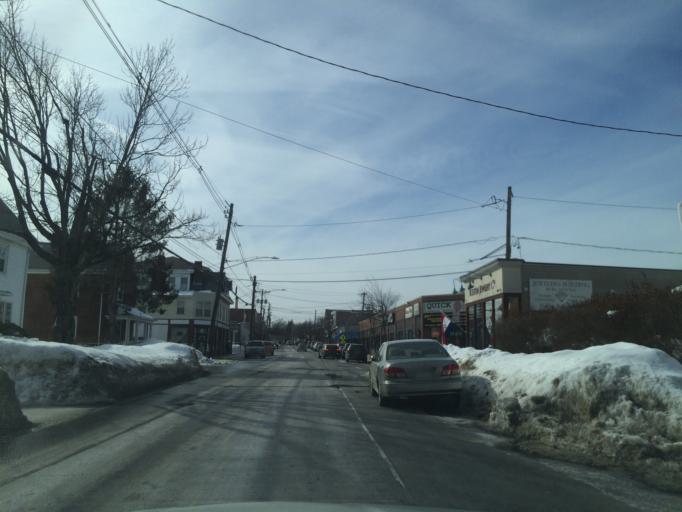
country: US
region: Massachusetts
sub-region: Middlesex County
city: Watertown
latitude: 42.3612
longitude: -71.1980
